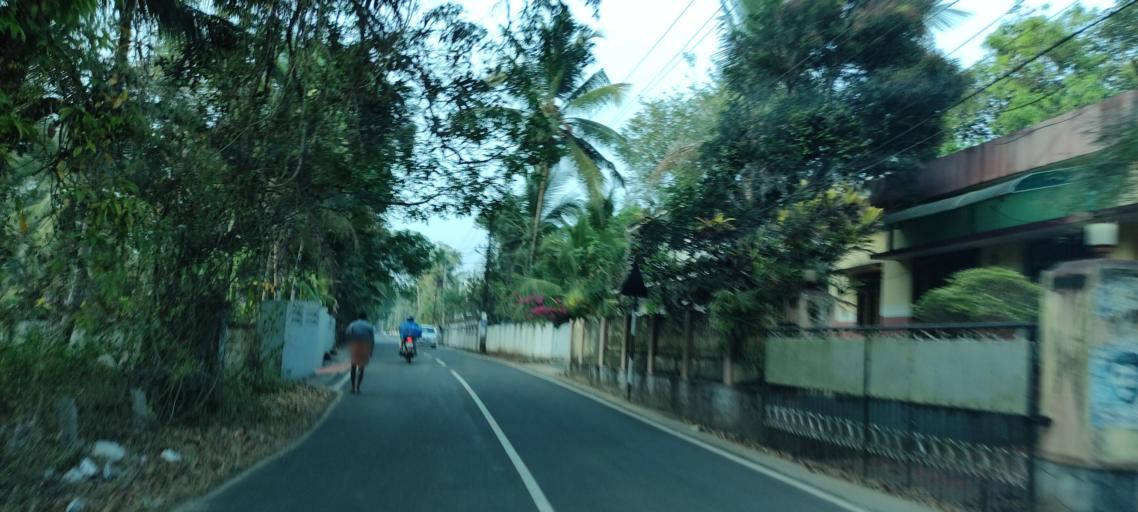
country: IN
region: Kerala
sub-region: Alappuzha
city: Mavelikara
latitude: 9.2636
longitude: 76.5563
